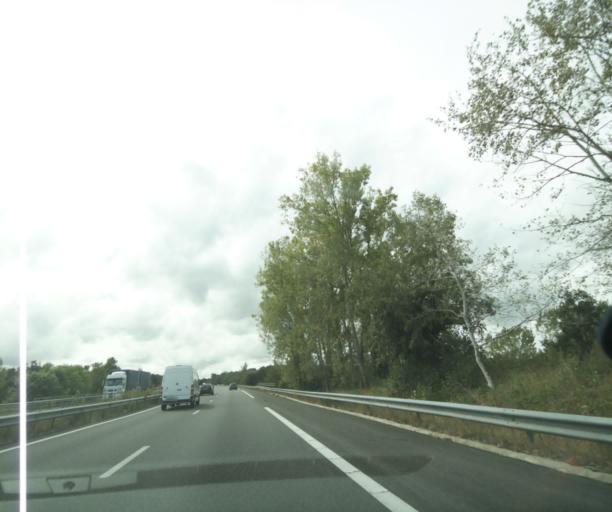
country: FR
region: Poitou-Charentes
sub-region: Departement de la Charente-Maritime
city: Saint-Genis-de-Saintonge
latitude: 45.4739
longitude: -0.6206
